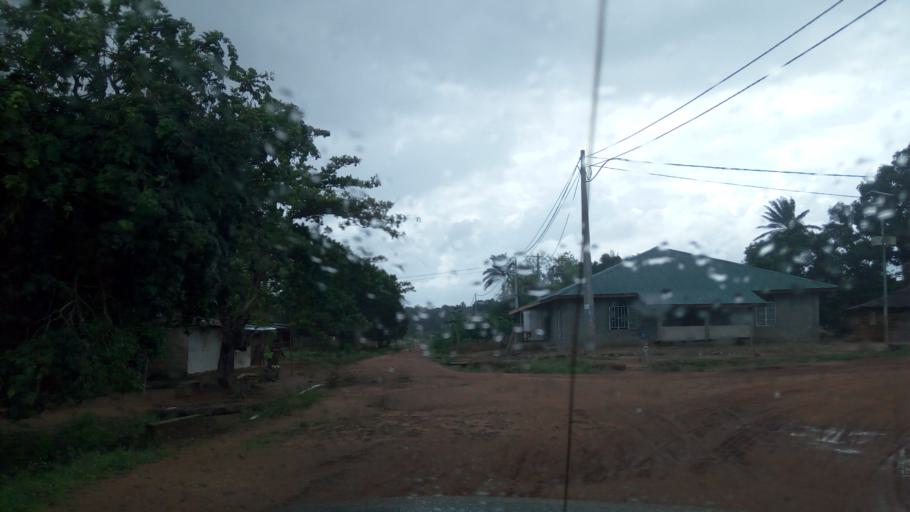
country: SL
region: Northern Province
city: Tintafor
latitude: 8.6401
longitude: -13.2219
